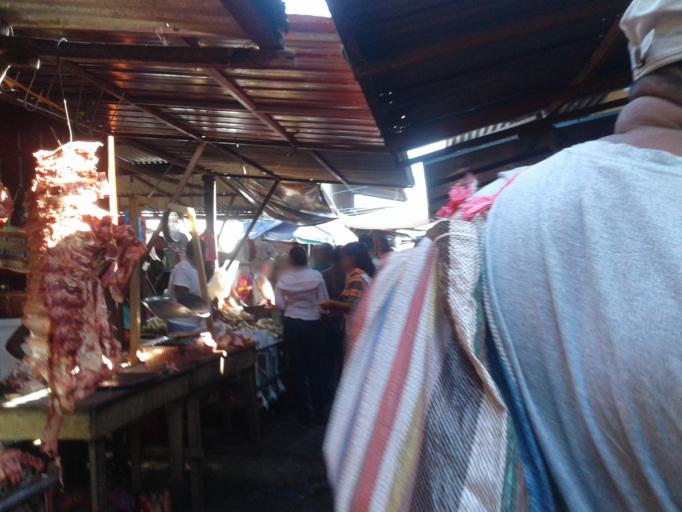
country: NI
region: Managua
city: Managua
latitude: 12.1484
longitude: -86.2625
